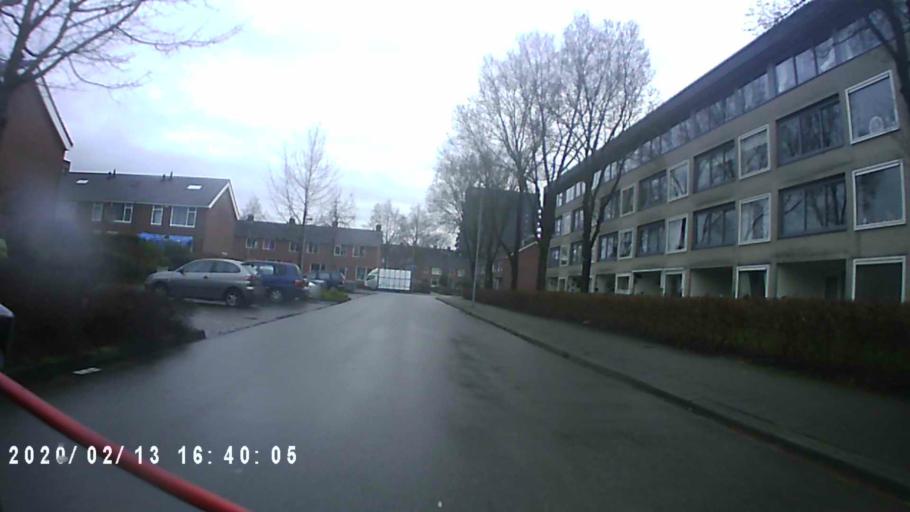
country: NL
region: Groningen
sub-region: Gemeente Groningen
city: Groningen
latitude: 53.2270
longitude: 6.5227
